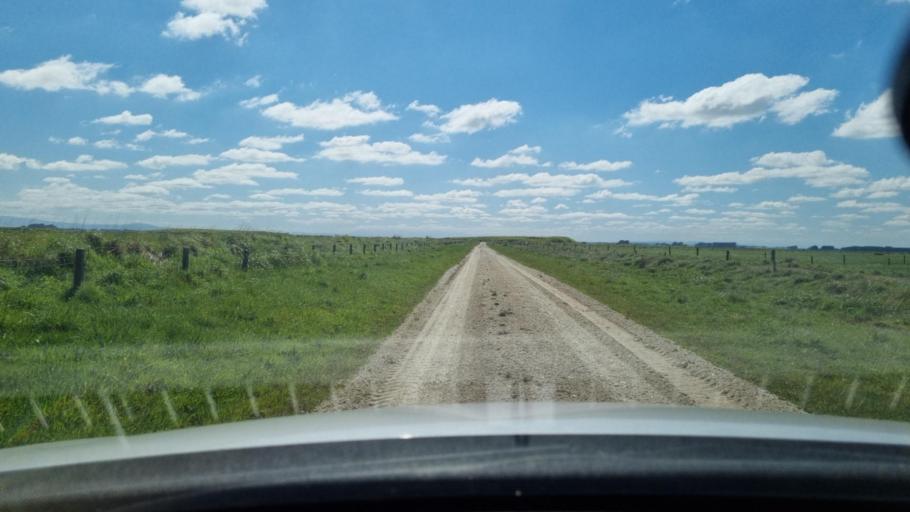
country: NZ
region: Southland
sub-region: Invercargill City
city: Invercargill
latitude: -46.3895
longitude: 168.2593
